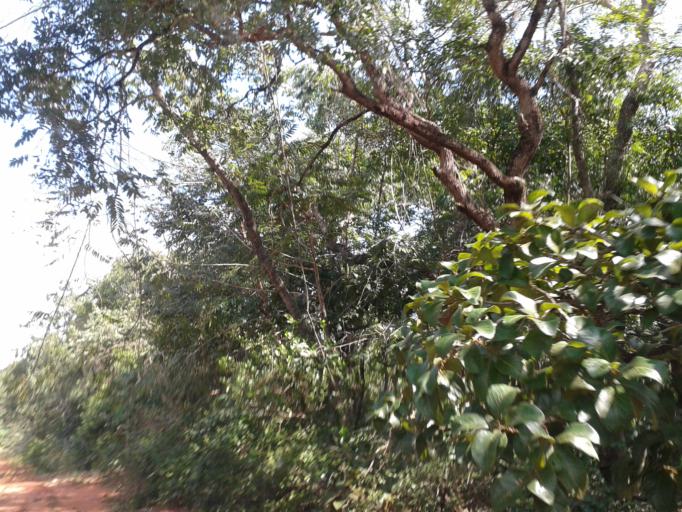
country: BR
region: Minas Gerais
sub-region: Campina Verde
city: Campina Verde
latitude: -19.3925
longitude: -49.6496
